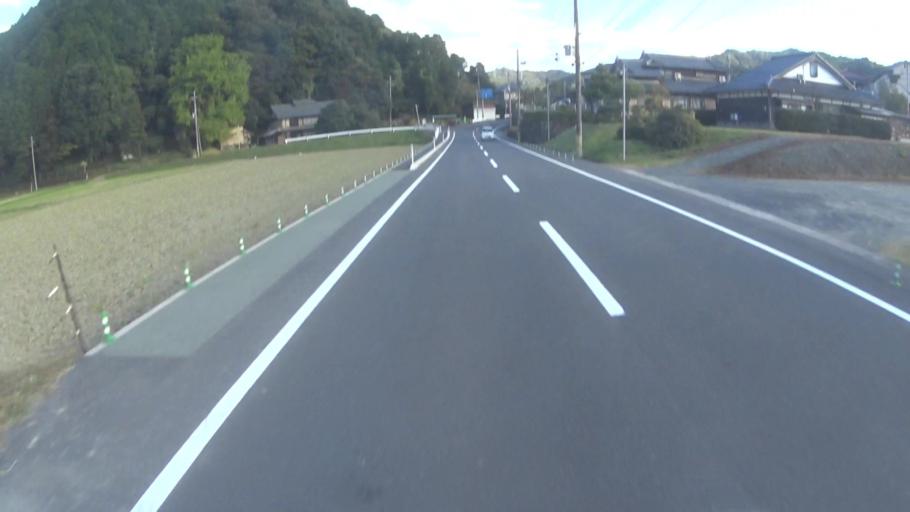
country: JP
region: Kyoto
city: Maizuru
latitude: 35.4308
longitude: 135.2305
